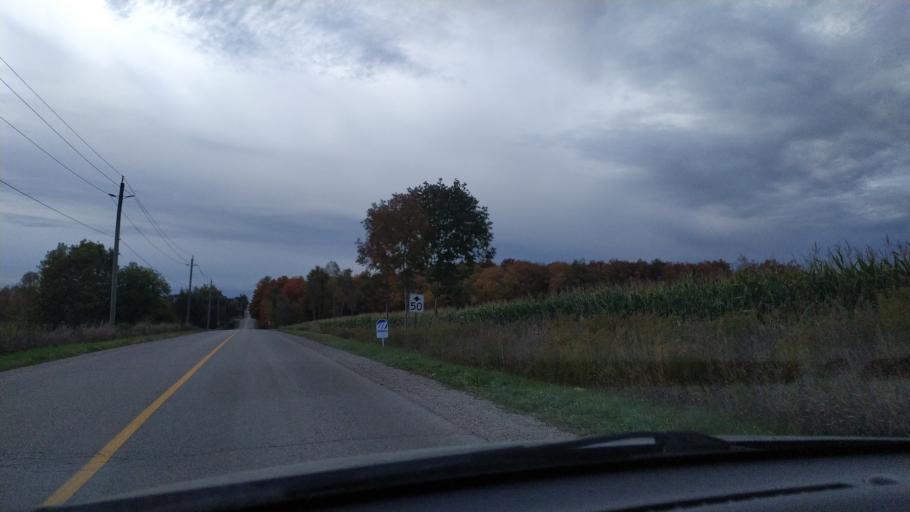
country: CA
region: Ontario
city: Waterloo
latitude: 43.5043
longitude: -80.6493
